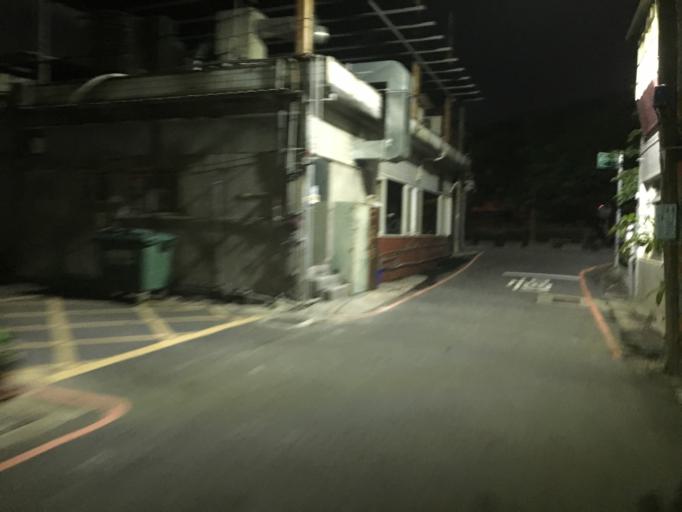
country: TW
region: Taiwan
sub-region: Hsinchu
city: Hsinchu
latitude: 24.8185
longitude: 120.9764
